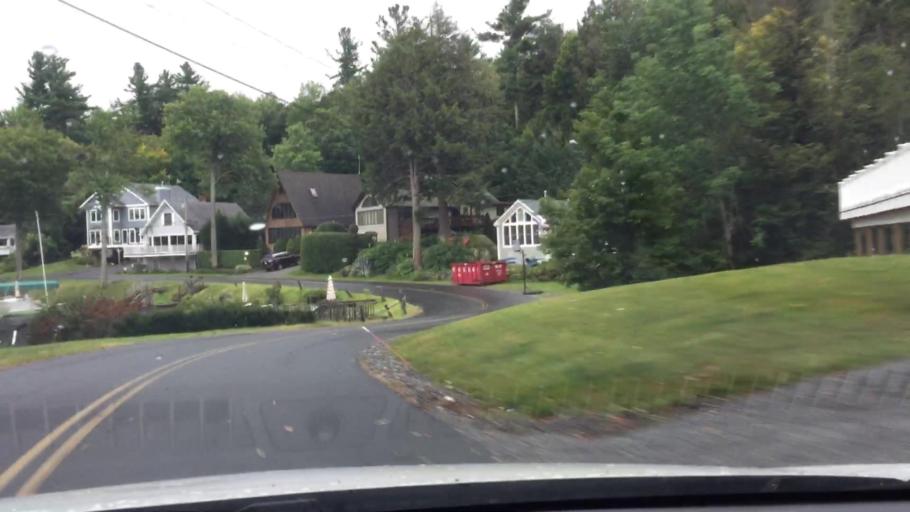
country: US
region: Massachusetts
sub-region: Berkshire County
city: Otis
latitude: 42.1513
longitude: -73.0561
